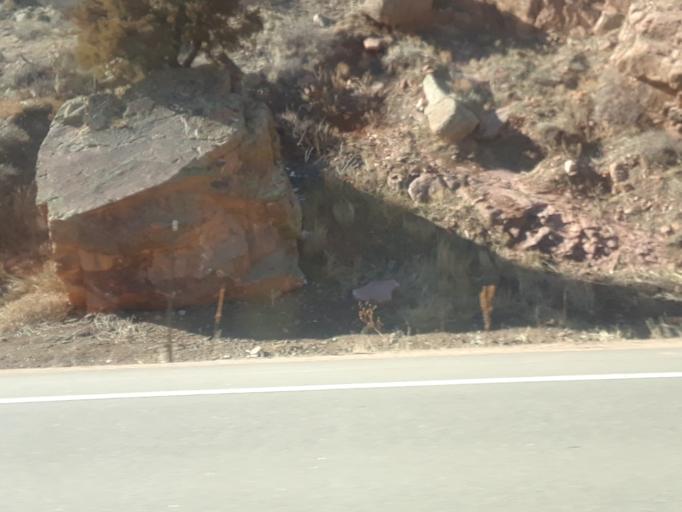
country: US
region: Colorado
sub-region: Boulder County
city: Lyons
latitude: 40.1265
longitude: -105.3047
